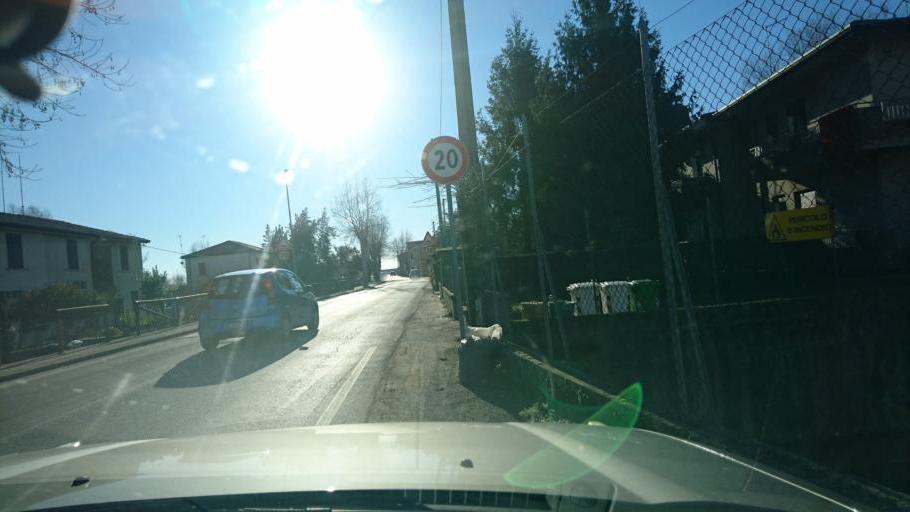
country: IT
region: Veneto
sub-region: Provincia di Rovigo
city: Loreo
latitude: 45.0606
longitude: 12.1944
